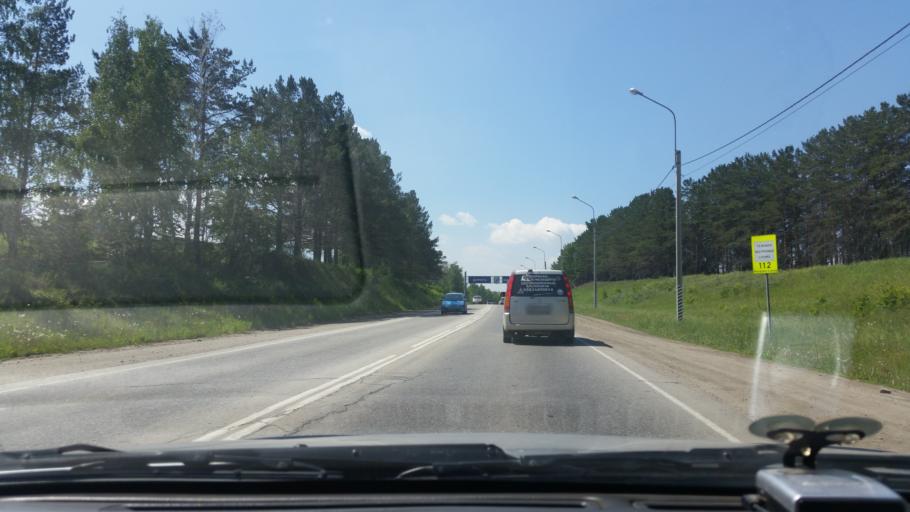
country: RU
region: Irkutsk
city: Smolenshchina
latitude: 52.2567
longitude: 104.1788
